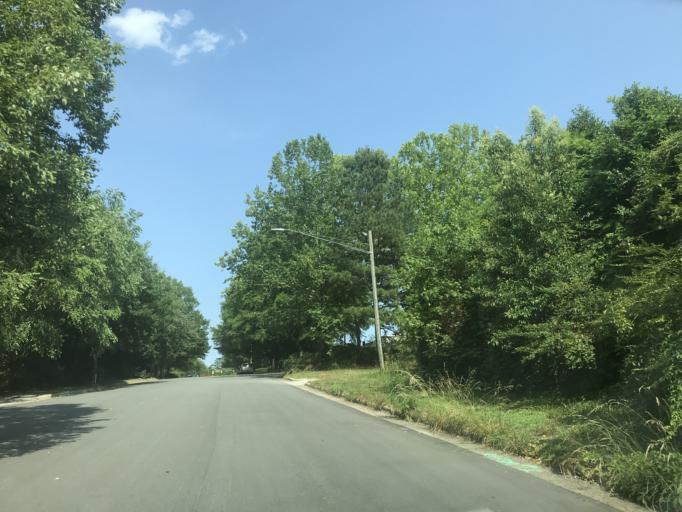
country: US
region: North Carolina
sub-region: Wake County
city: West Raleigh
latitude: 35.8999
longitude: -78.6840
